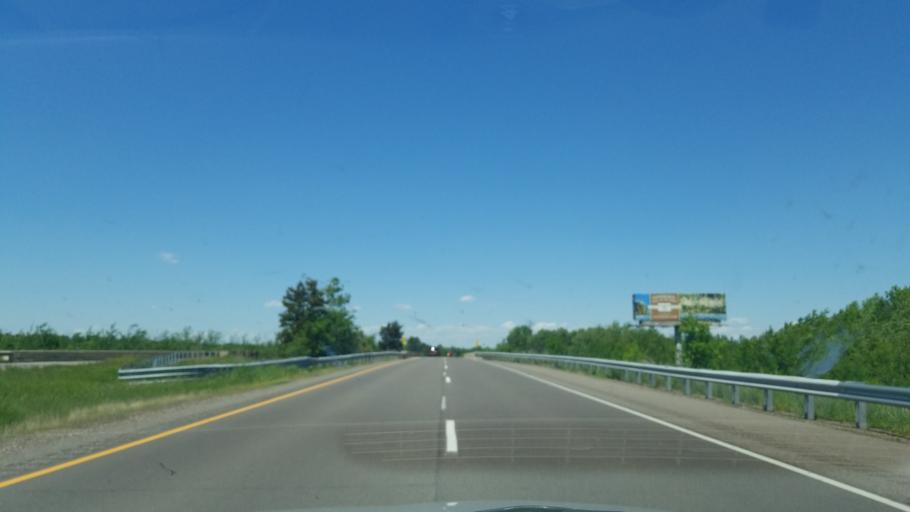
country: US
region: Minnesota
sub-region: Pine County
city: Hinckley
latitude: 46.0313
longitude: -92.9251
